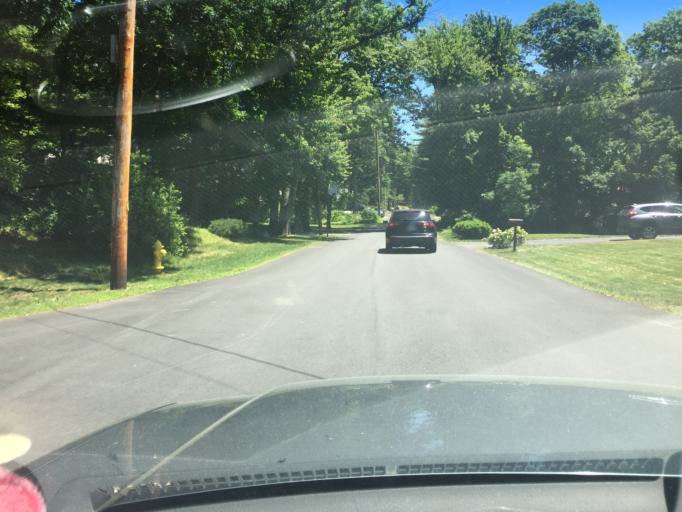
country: US
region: Massachusetts
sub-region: Norfolk County
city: Westwood
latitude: 42.2175
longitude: -71.2313
